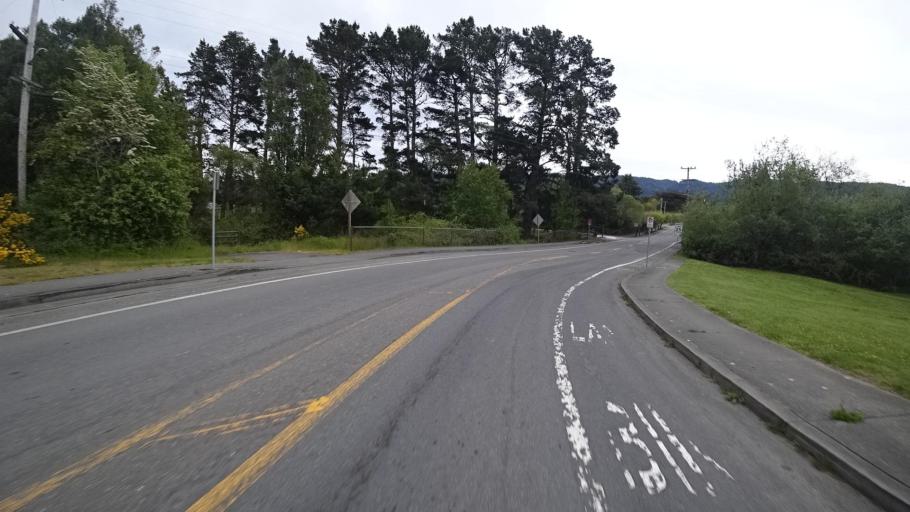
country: US
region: California
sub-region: Humboldt County
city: Blue Lake
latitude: 40.8861
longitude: -123.9955
